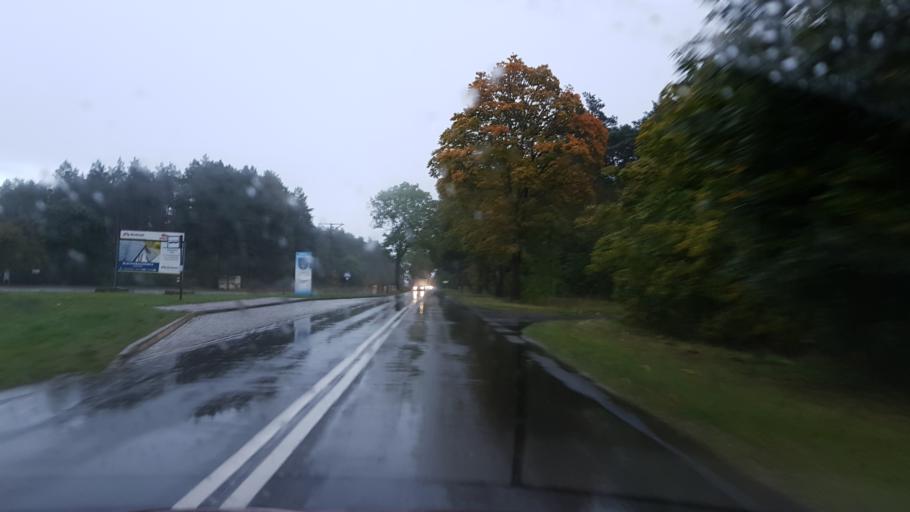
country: PL
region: Greater Poland Voivodeship
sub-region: Powiat pilski
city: Szydlowo
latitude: 53.1569
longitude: 16.6682
